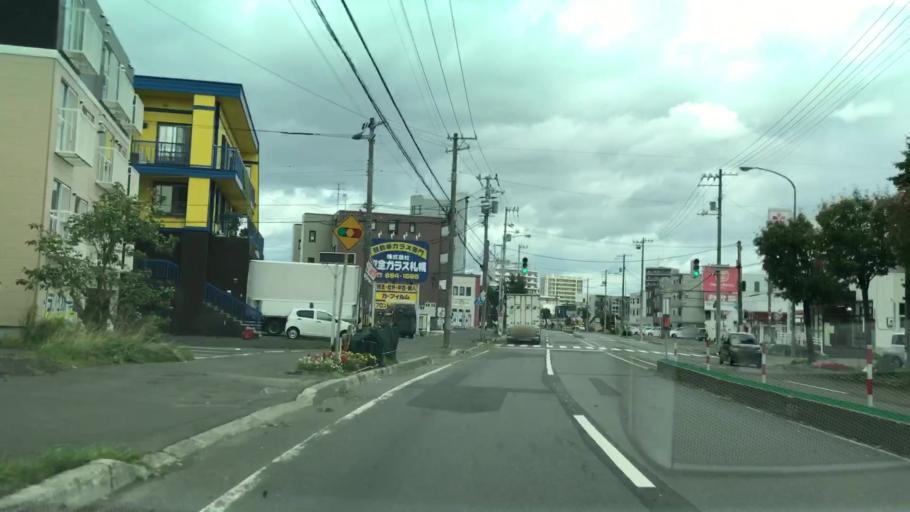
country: JP
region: Hokkaido
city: Sapporo
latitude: 42.9930
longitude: 141.4407
